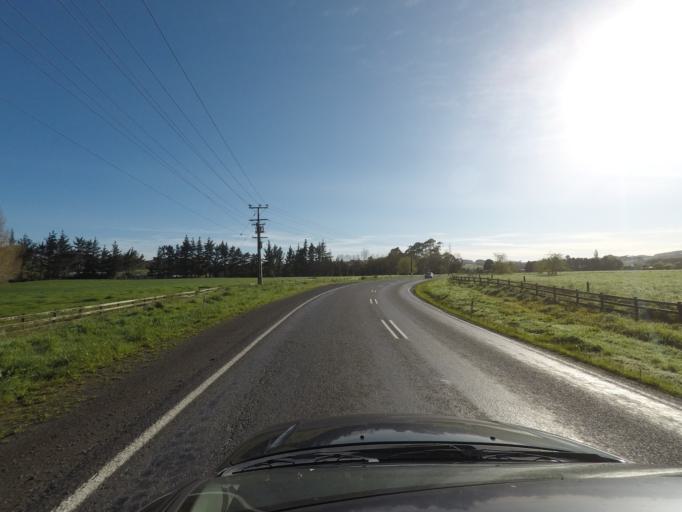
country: NZ
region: Auckland
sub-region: Auckland
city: Red Hill
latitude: -37.0031
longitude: 174.9570
